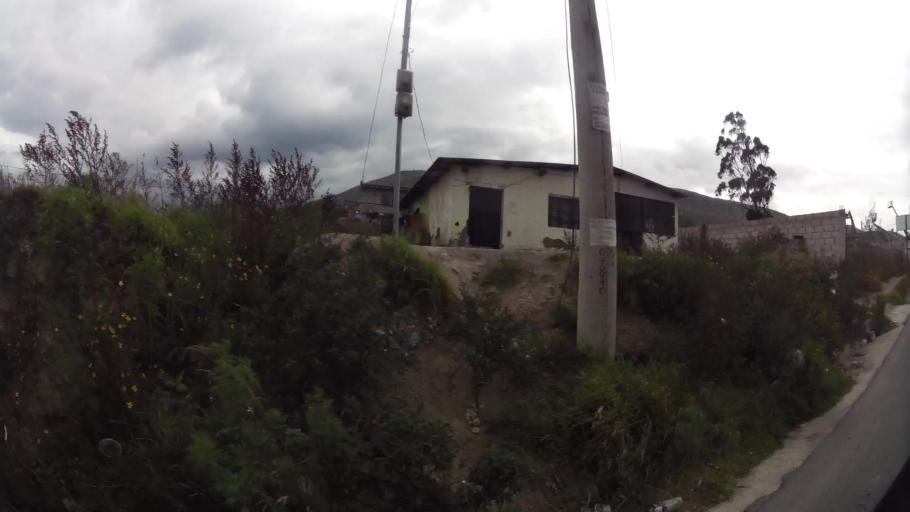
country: EC
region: Pichincha
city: Quito
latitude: 0.0008
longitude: -78.4572
